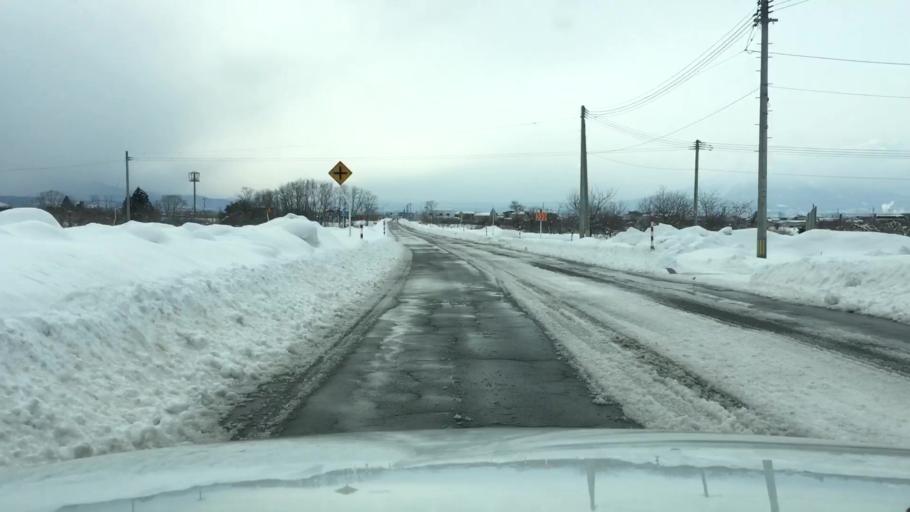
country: JP
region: Aomori
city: Kuroishi
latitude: 40.5933
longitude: 140.5962
